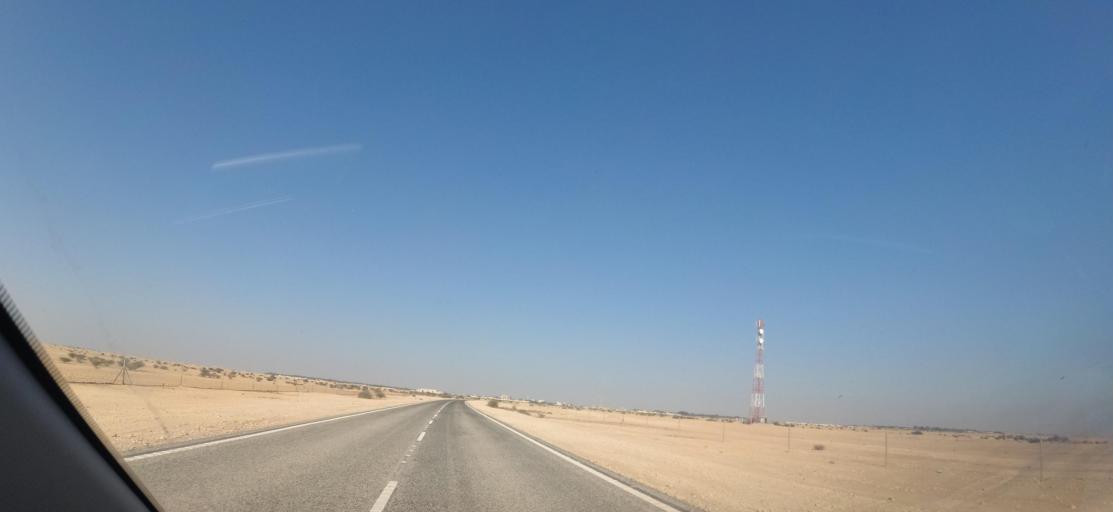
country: QA
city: Al Ghuwayriyah
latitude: 25.8135
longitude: 51.2309
